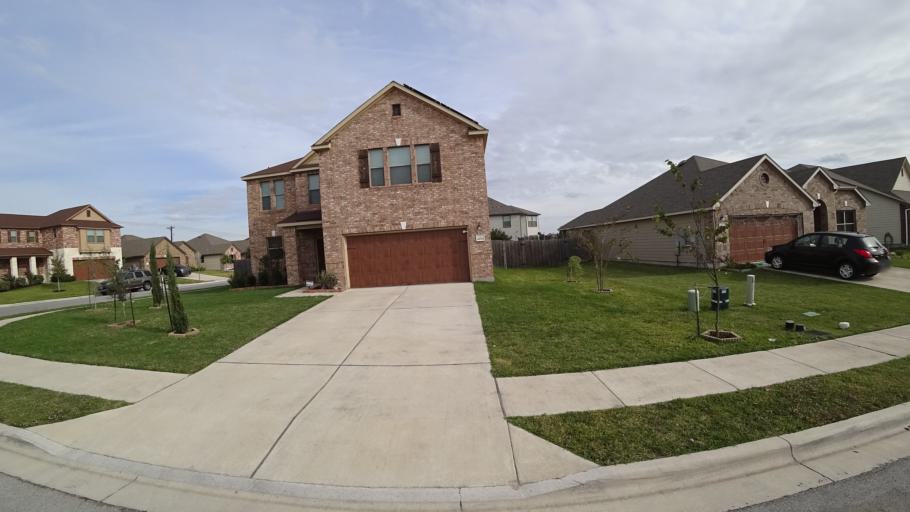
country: US
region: Texas
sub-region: Travis County
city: Wells Branch
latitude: 30.4329
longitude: -97.6633
